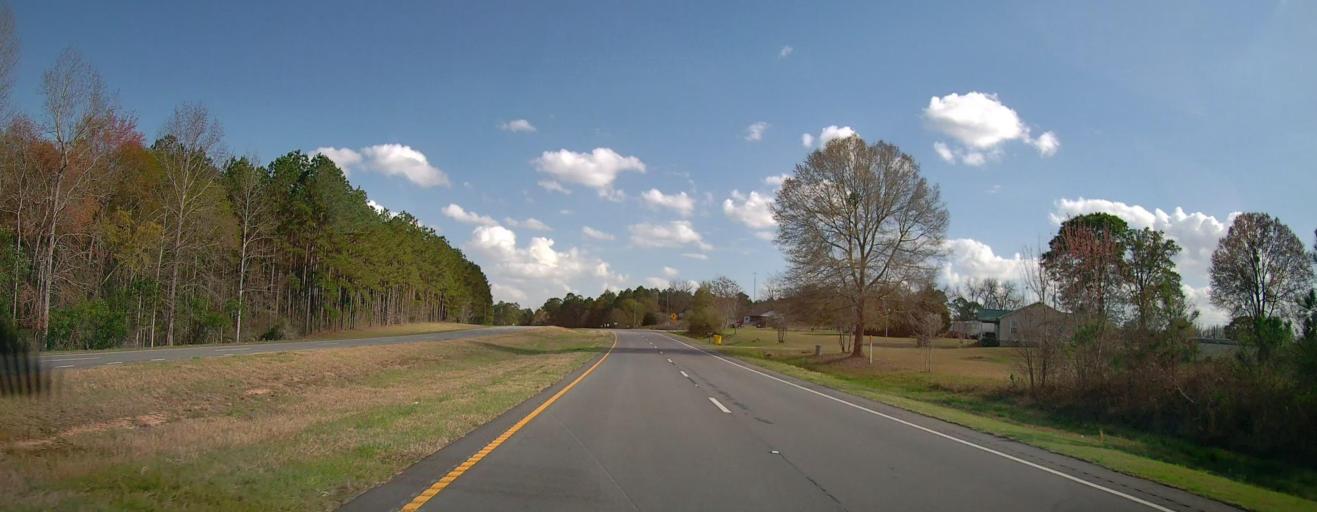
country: US
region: Georgia
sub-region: Telfair County
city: McRae
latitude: 32.0465
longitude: -82.8579
